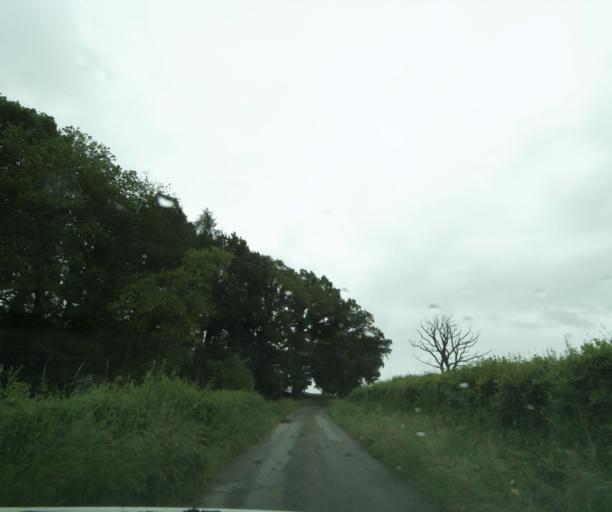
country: FR
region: Bourgogne
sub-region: Departement de Saone-et-Loire
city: Charolles
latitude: 46.4904
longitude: 4.2468
